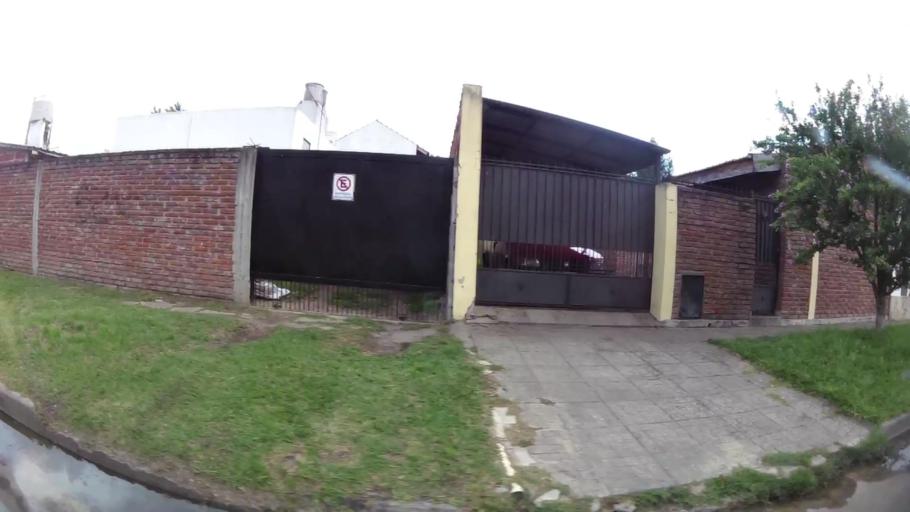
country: AR
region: Buenos Aires
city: Ituzaingo
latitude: -34.6375
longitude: -58.6852
